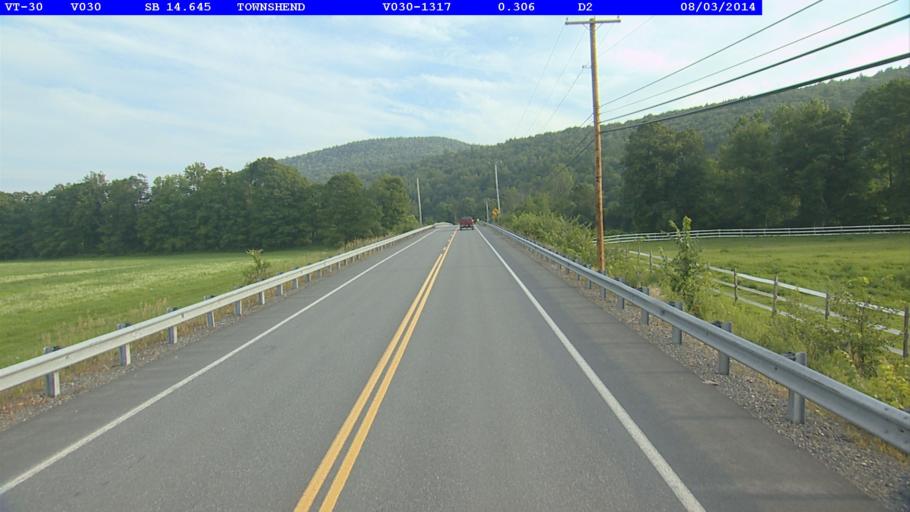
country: US
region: Vermont
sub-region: Windham County
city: Newfane
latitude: 43.0237
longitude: -72.6569
